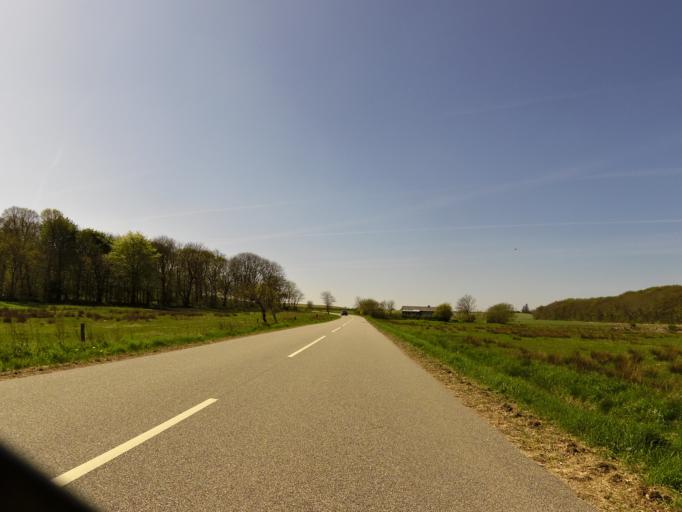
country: DK
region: Central Jutland
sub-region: Struer Kommune
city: Struer
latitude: 56.5172
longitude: 8.5975
